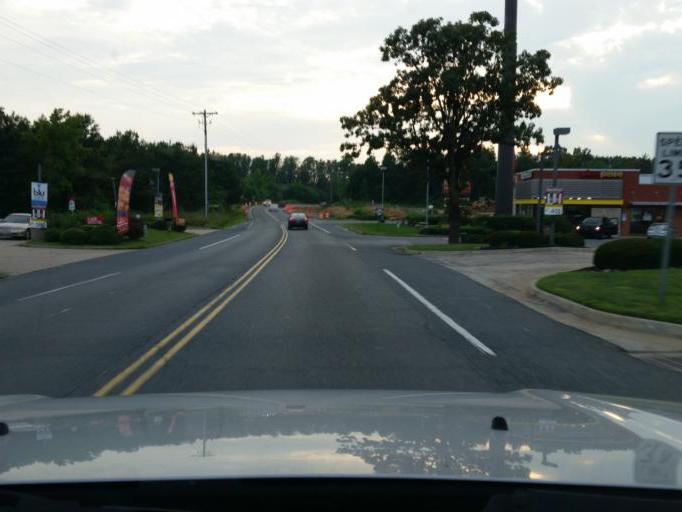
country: US
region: Virginia
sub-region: Spotsylvania County
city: Spotsylvania Courthouse
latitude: 38.1324
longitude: -77.5132
